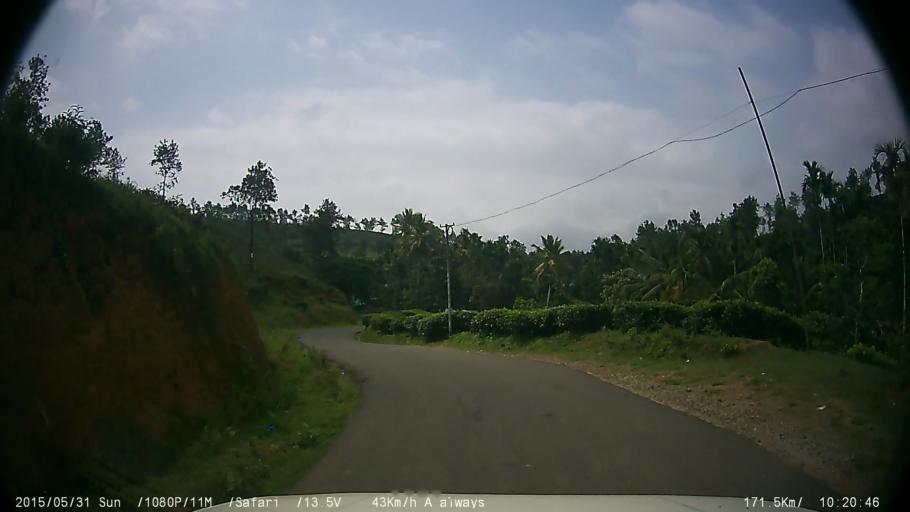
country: IN
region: Kerala
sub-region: Wayanad
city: Kalpetta
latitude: 11.5439
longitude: 76.1378
